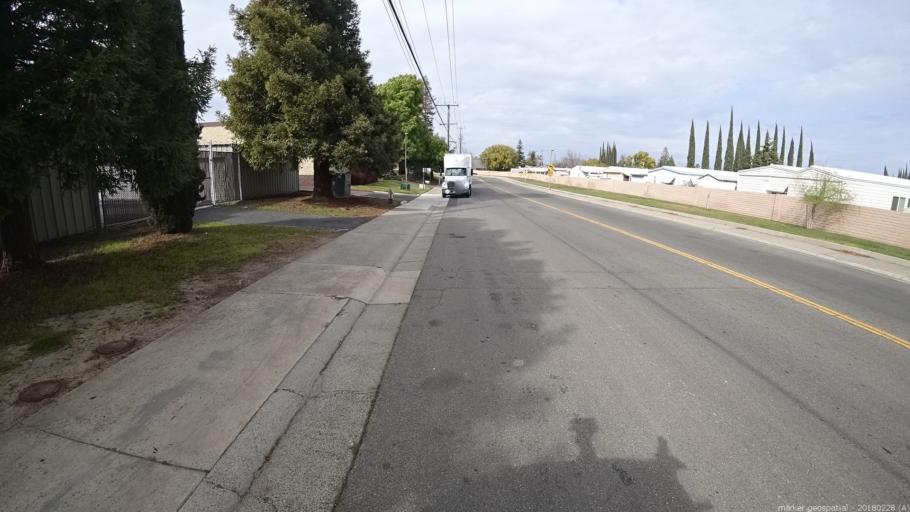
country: US
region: California
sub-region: Sacramento County
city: Antelope
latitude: 38.7044
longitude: -121.3264
